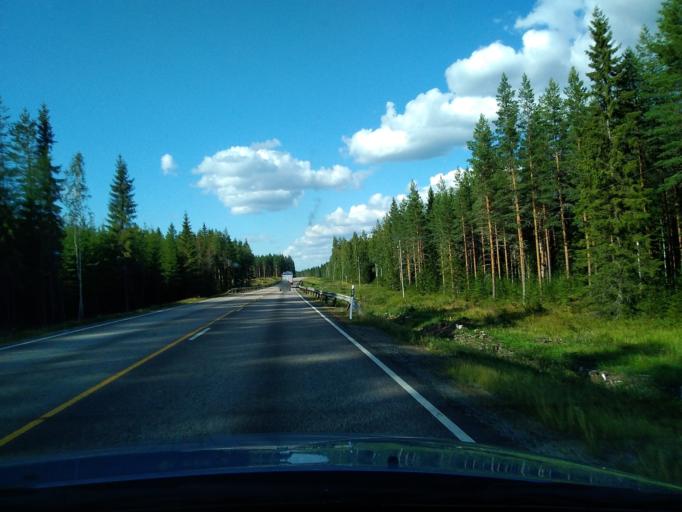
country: FI
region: Pirkanmaa
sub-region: Ylae-Pirkanmaa
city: Maenttae
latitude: 62.0797
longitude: 24.7256
